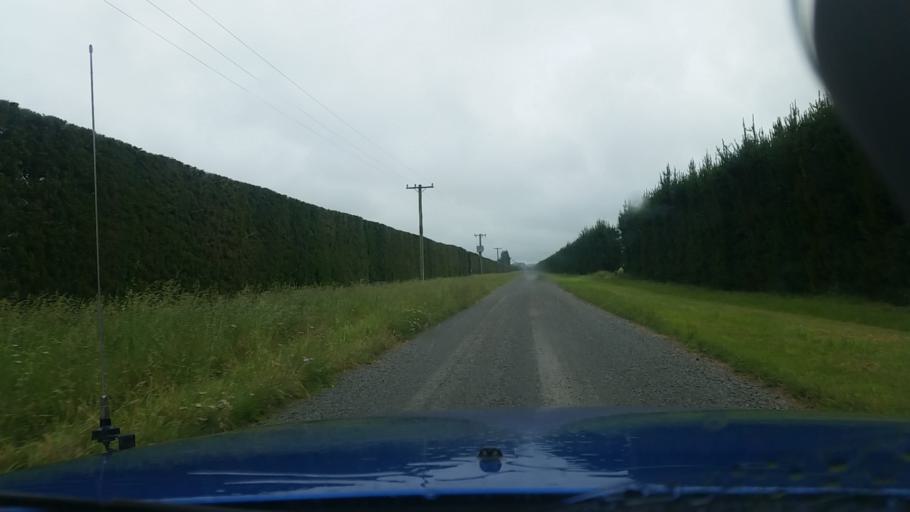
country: NZ
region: Canterbury
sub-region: Ashburton District
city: Tinwald
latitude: -43.9019
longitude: 171.5626
